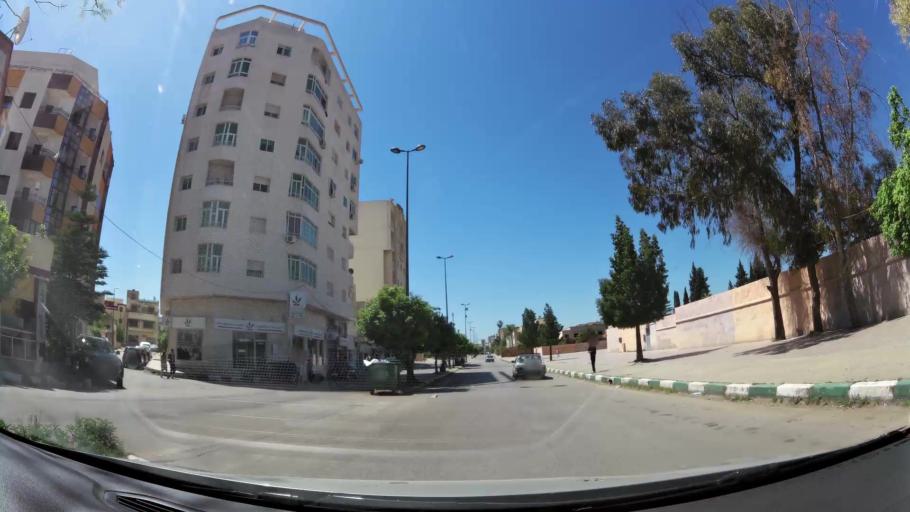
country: MA
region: Meknes-Tafilalet
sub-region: Meknes
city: Meknes
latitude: 33.9057
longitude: -5.5325
